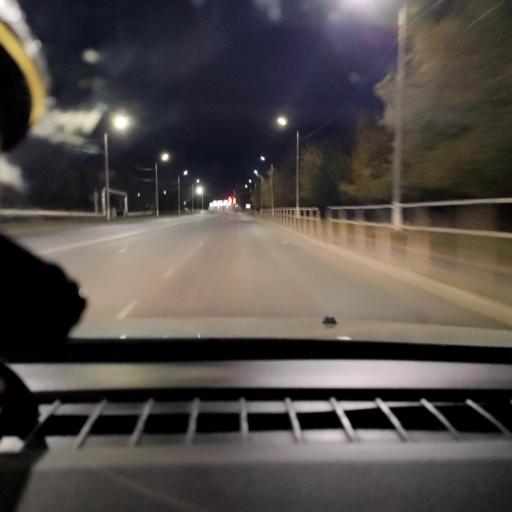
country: RU
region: Samara
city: Novokuybyshevsk
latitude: 53.0926
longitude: 49.9406
